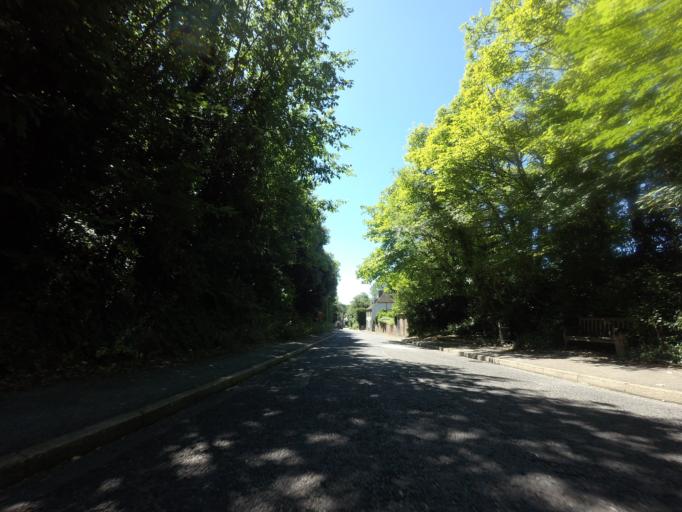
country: GB
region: England
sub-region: Kent
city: Eastry
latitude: 51.2428
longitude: 1.3078
